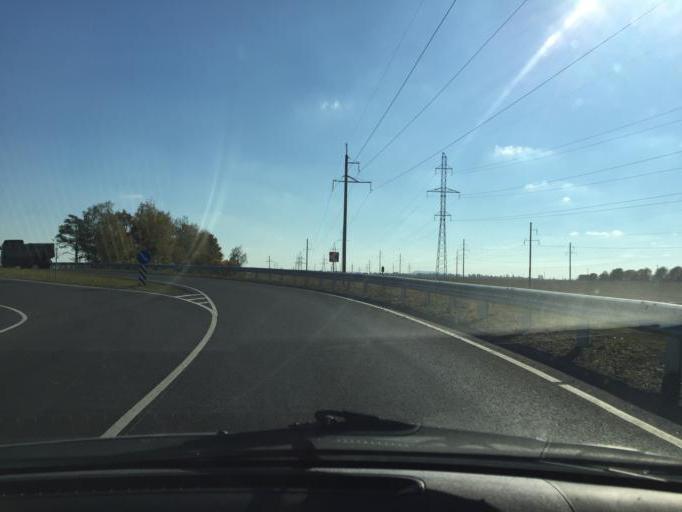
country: BY
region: Minsk
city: Slutsk
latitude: 53.0087
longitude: 27.4863
